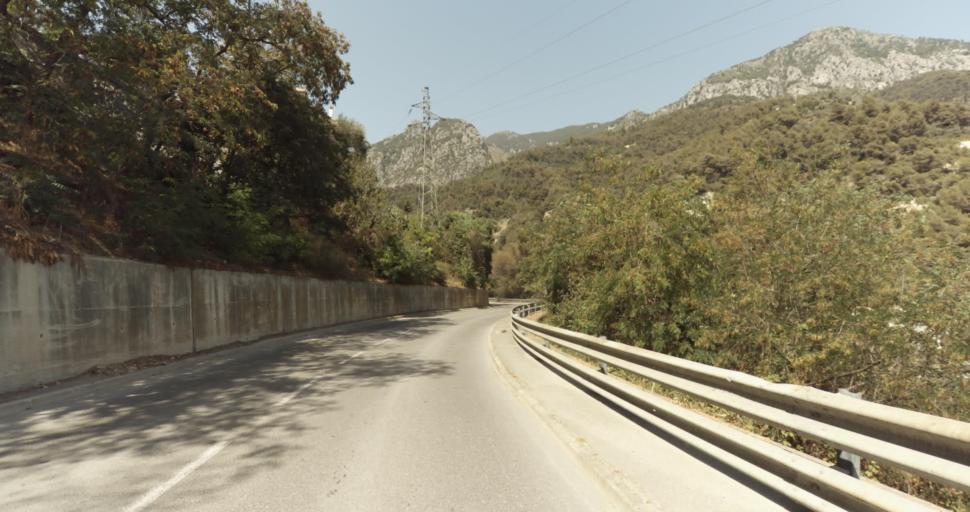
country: FR
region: Provence-Alpes-Cote d'Azur
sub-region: Departement des Alpes-Maritimes
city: Sainte-Agnes
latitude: 43.8057
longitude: 7.4860
